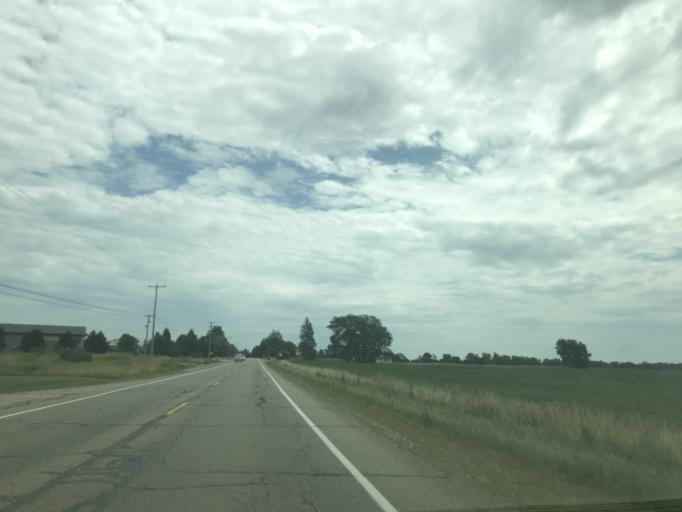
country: US
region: Michigan
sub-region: Clinton County
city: Wacousta
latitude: 42.7955
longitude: -84.7268
